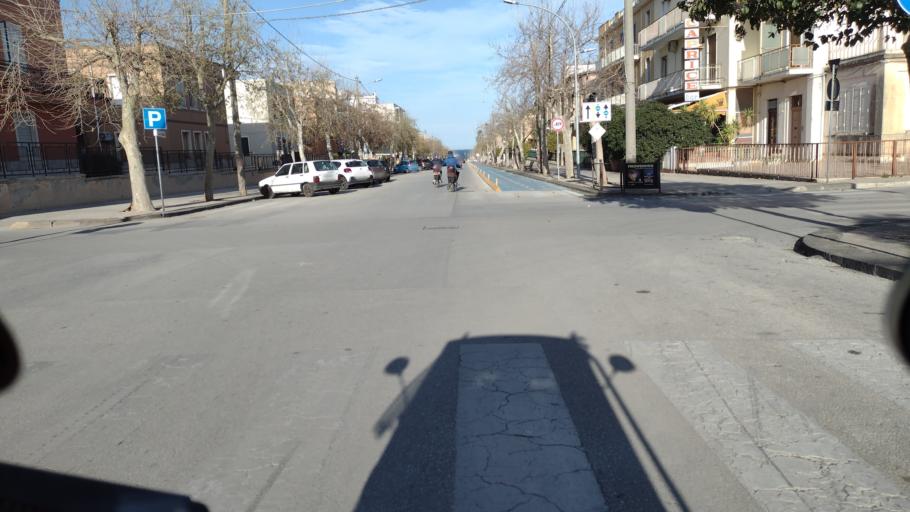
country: IT
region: Sicily
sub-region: Provincia di Siracusa
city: Avola
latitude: 36.9109
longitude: 15.1408
